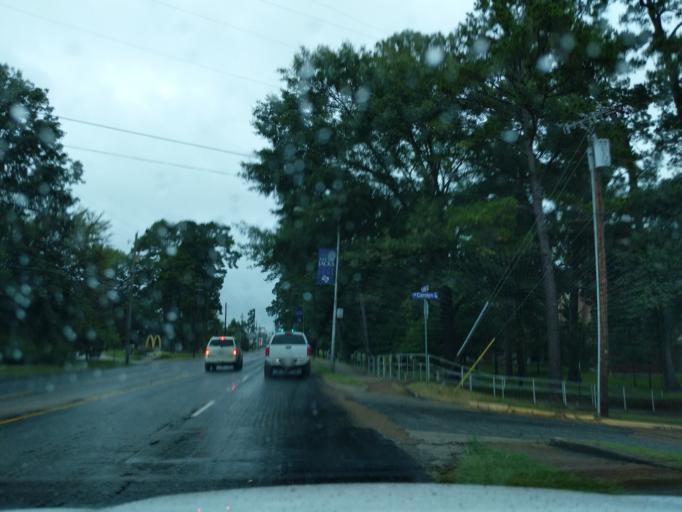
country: US
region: Texas
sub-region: Nacogdoches County
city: Nacogdoches
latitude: 31.6175
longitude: -94.6527
